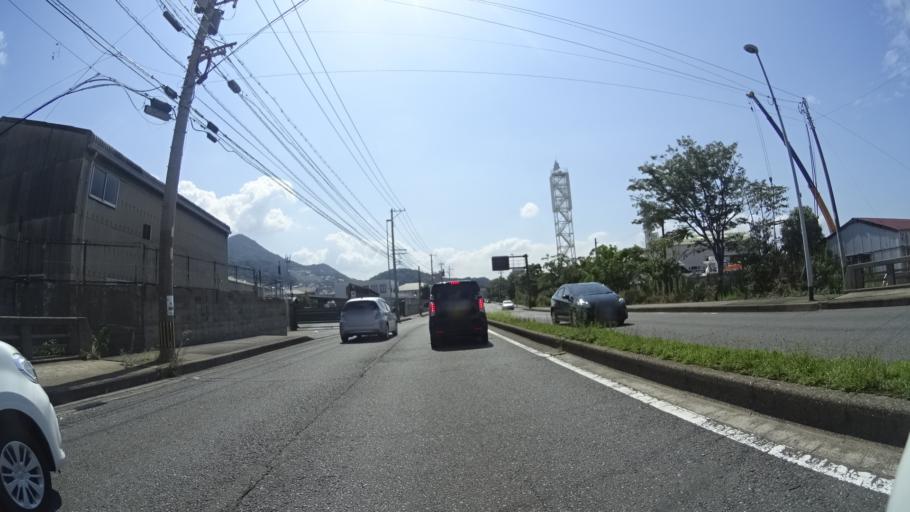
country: JP
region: Yamaguchi
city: Shimonoseki
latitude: 33.8981
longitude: 130.9221
